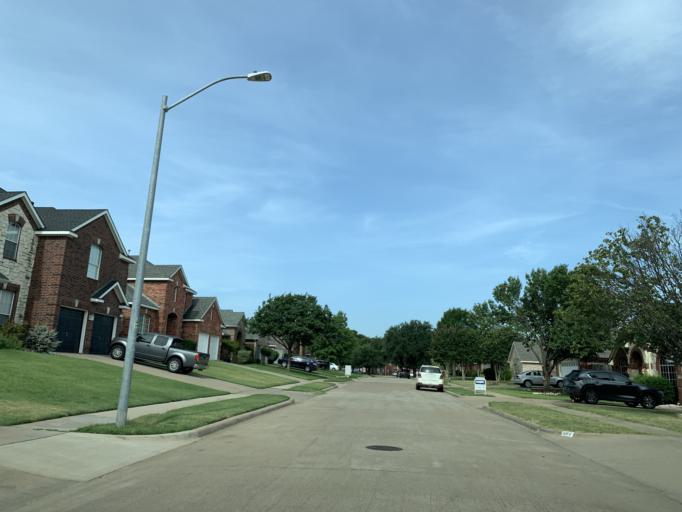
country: US
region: Texas
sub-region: Dallas County
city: Grand Prairie
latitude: 32.6690
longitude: -97.0120
